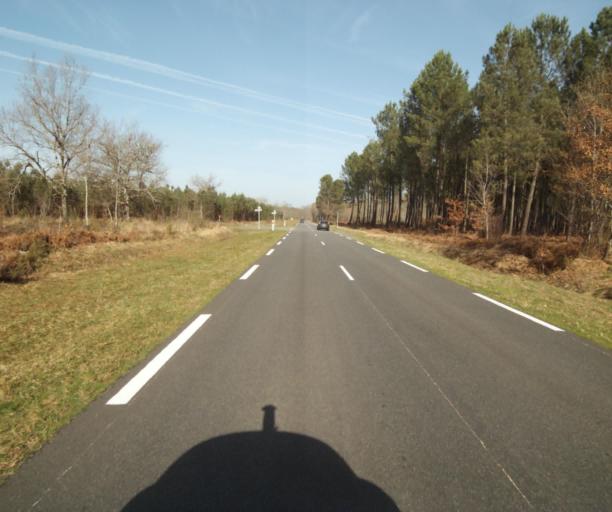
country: FR
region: Aquitaine
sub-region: Departement de la Gironde
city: Grignols
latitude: 44.1921
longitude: -0.1236
